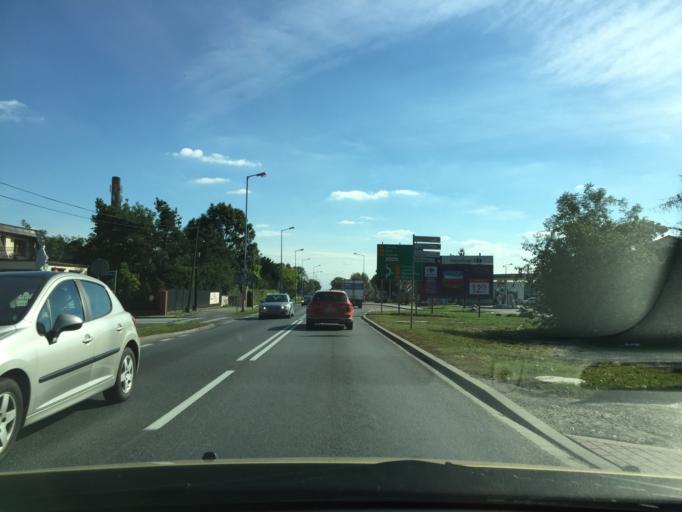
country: PL
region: Greater Poland Voivodeship
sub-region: Kalisz
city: Kalisz
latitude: 51.7852
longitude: 18.0899
